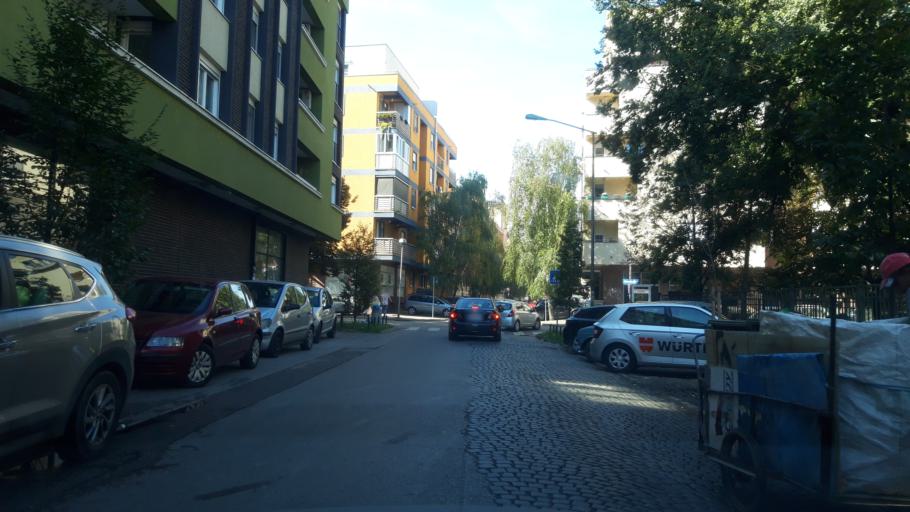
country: RS
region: Autonomna Pokrajina Vojvodina
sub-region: Juznobacki Okrug
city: Novi Sad
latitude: 45.2596
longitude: 19.8512
